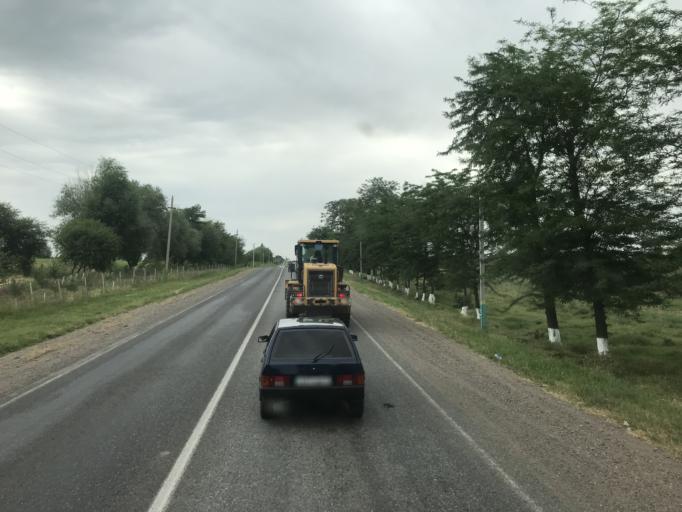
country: UZ
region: Toshkent
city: Salor
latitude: 41.4956
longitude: 69.3332
